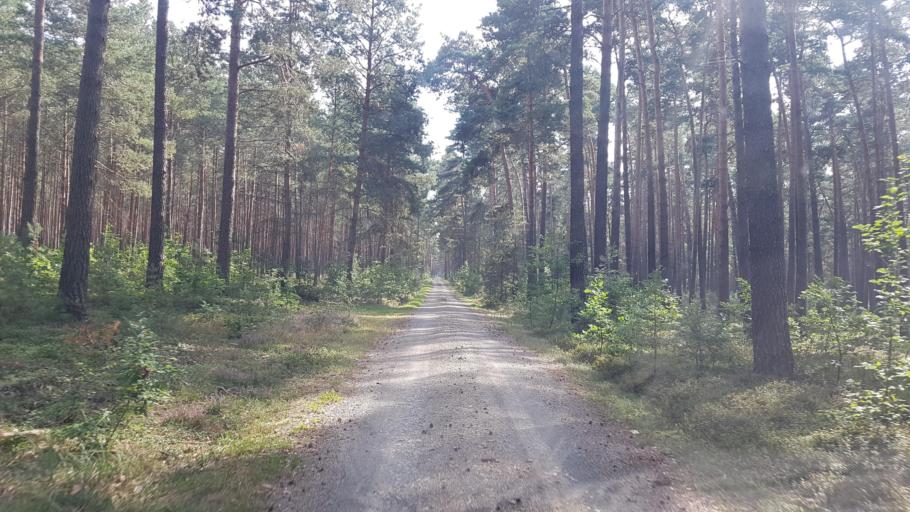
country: DE
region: Brandenburg
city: Hohenbucko
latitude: 51.7870
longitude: 13.5213
